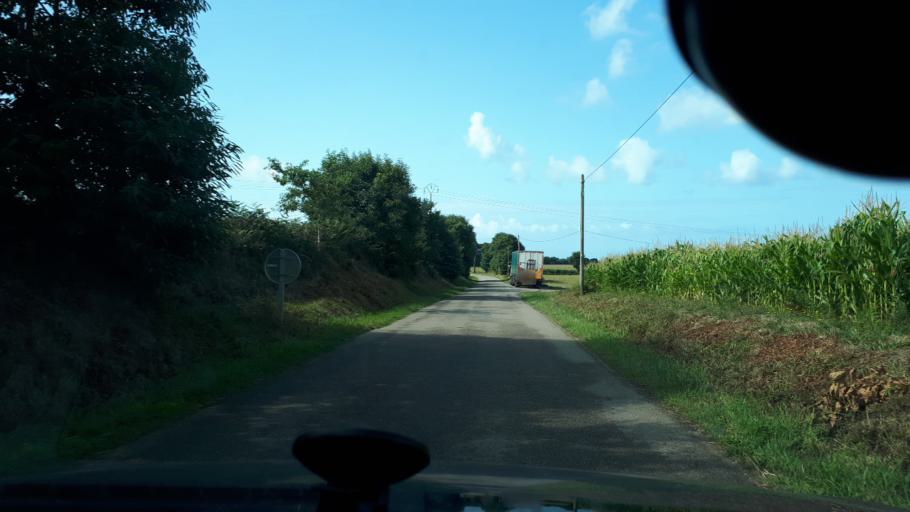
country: FR
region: Brittany
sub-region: Departement du Finistere
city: Pouldreuzic
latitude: 47.9847
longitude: -4.3680
